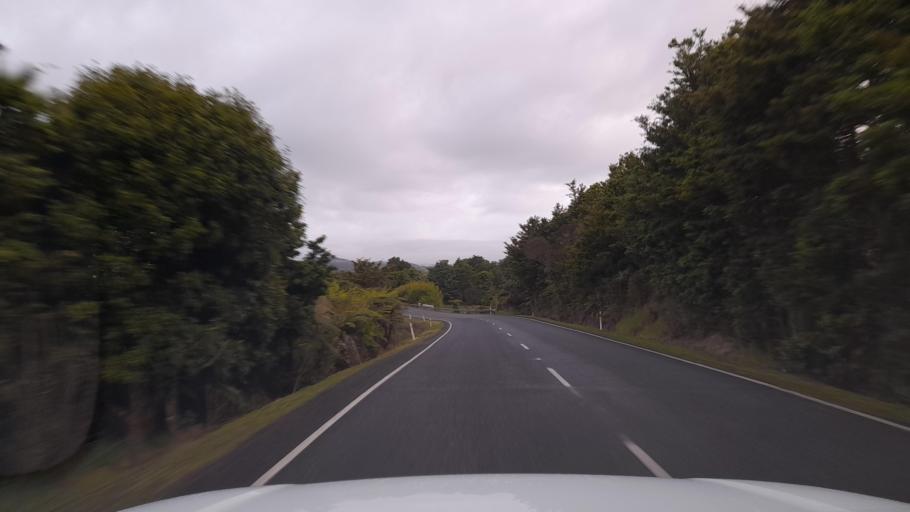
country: NZ
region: Northland
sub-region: Whangarei
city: Maungatapere
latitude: -35.7242
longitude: 174.0425
